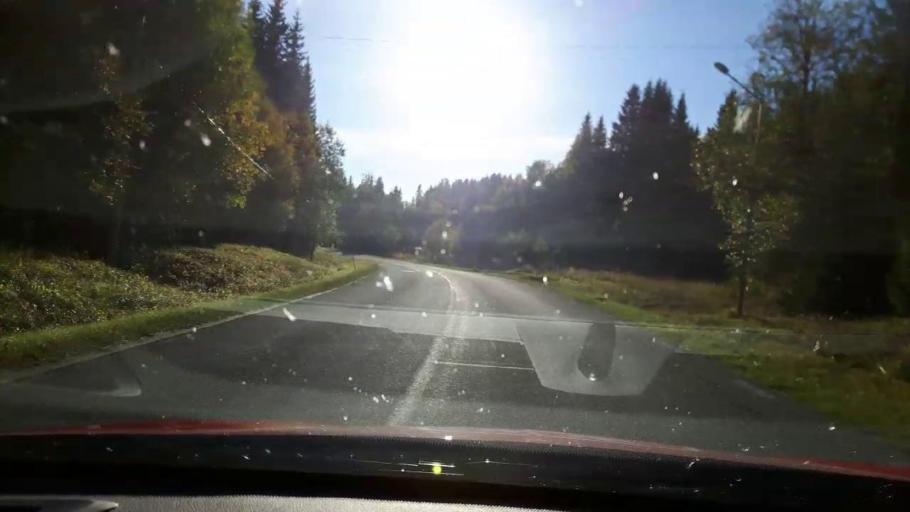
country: SE
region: Jaemtland
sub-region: OEstersunds Kommun
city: Lit
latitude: 63.8186
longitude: 14.8172
